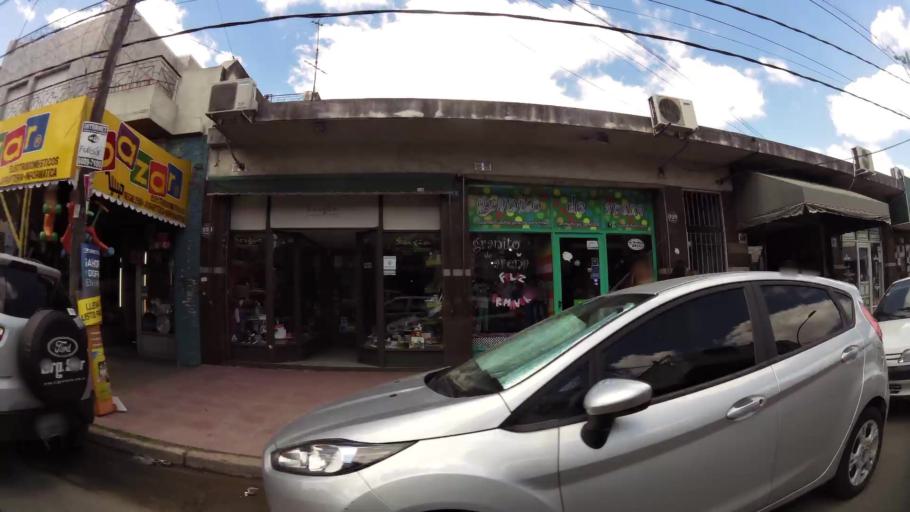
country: AR
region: Buenos Aires
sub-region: Partido de Lanus
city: Lanus
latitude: -34.7103
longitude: -58.4218
